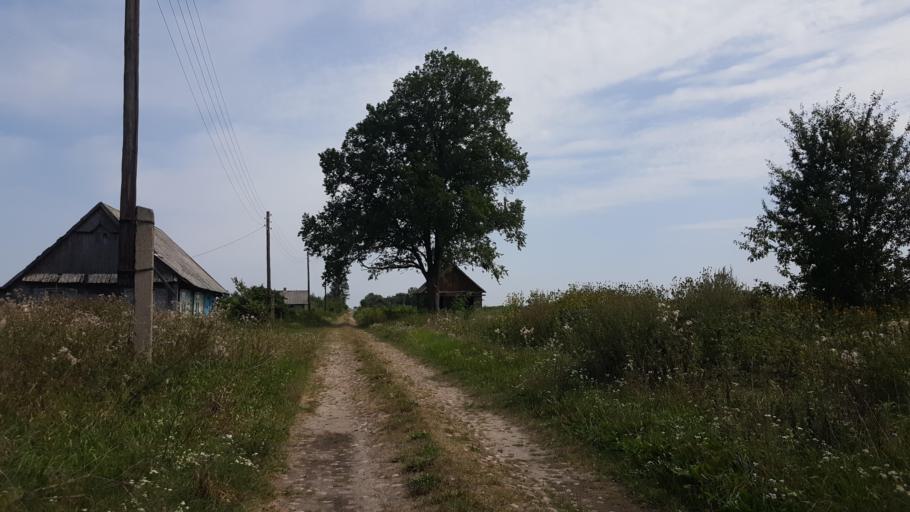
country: BY
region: Brest
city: Kamyanyets
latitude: 52.4520
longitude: 23.6505
